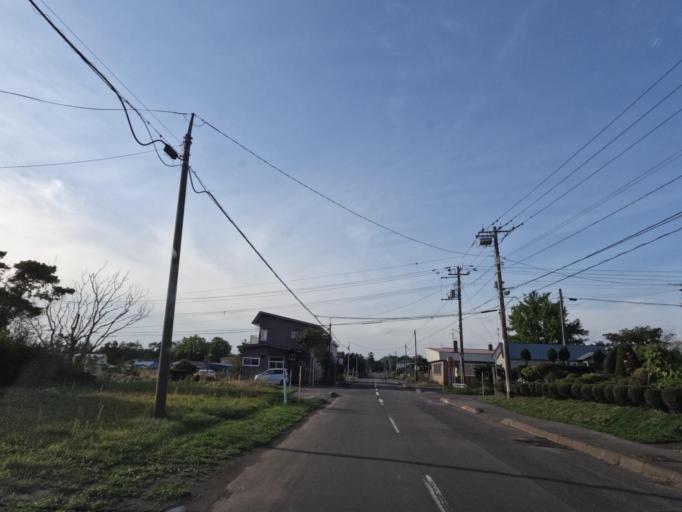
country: JP
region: Hokkaido
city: Date
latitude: 42.4217
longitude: 140.9101
